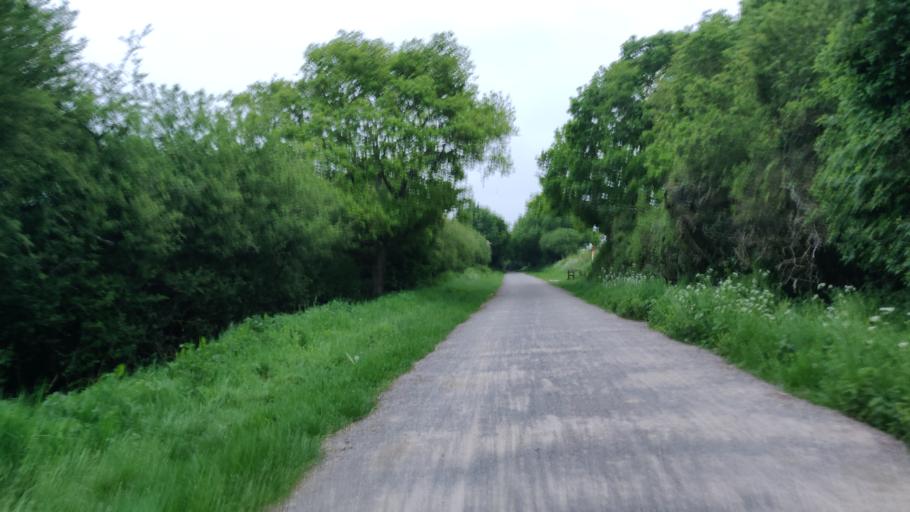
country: GB
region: England
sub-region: West Sussex
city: Partridge Green
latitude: 50.9712
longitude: -0.3156
